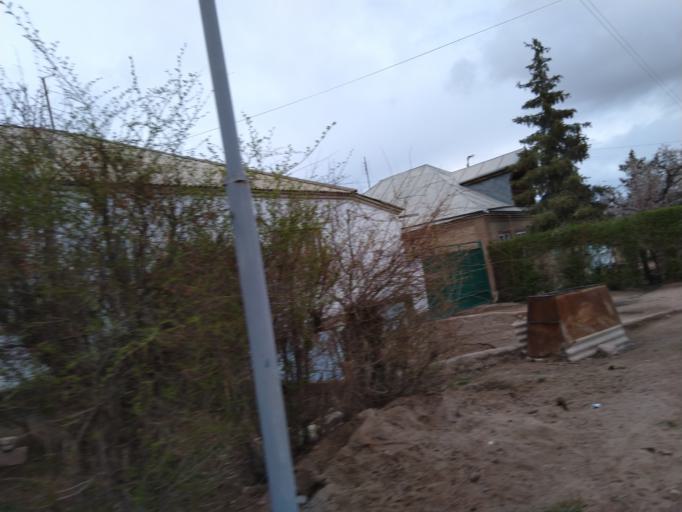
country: KG
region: Ysyk-Koel
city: Bokombayevskoye
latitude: 42.1113
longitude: 76.9830
